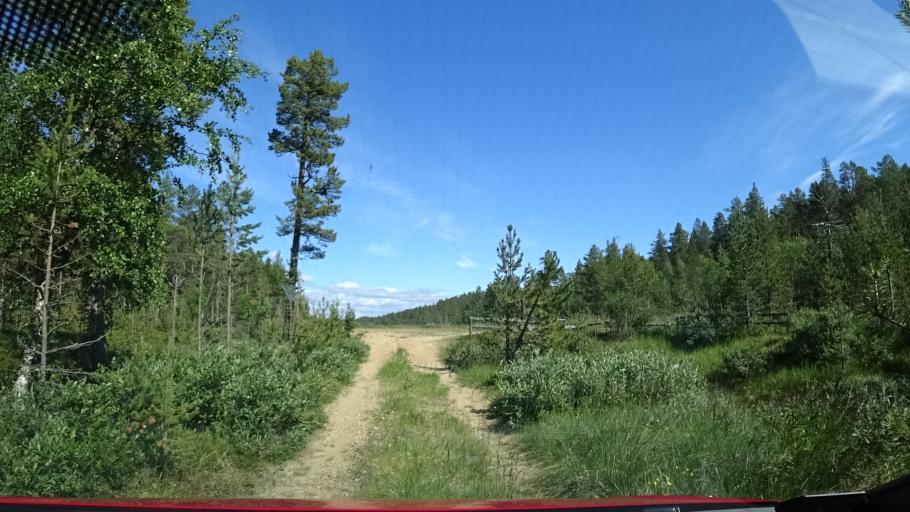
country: FI
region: Lapland
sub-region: Pohjois-Lappi
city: Inari
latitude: 68.7783
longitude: 26.5433
